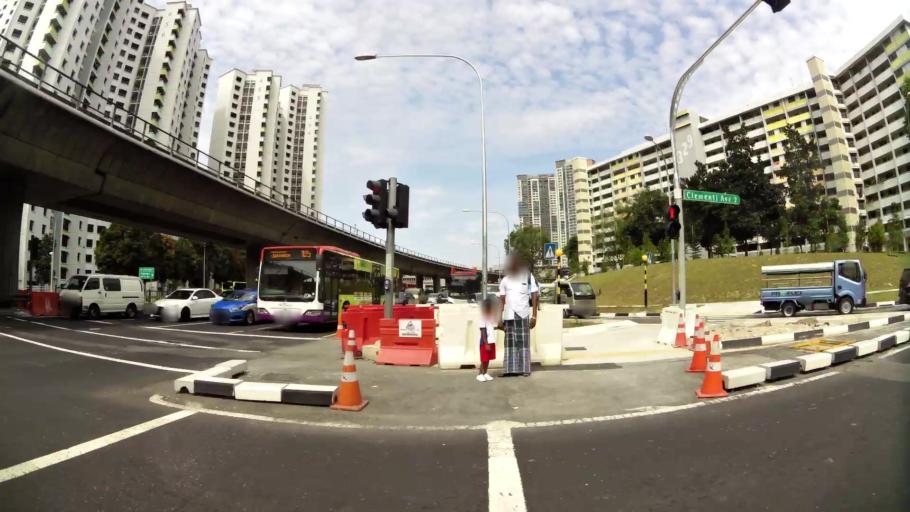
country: SG
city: Singapore
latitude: 1.3123
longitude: 103.7679
